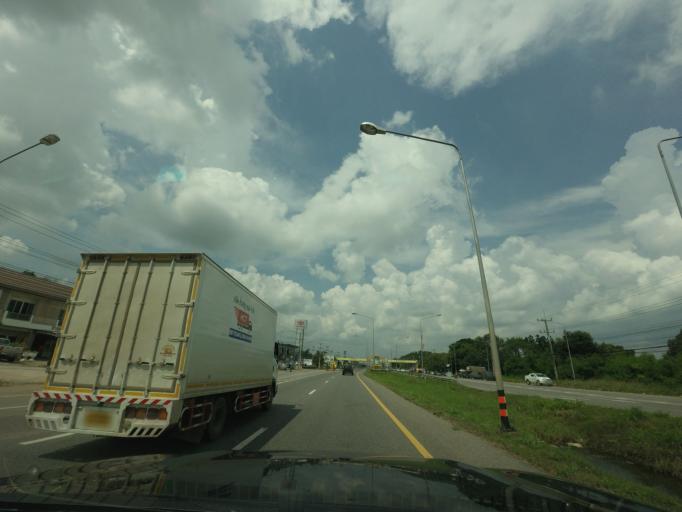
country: TH
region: Khon Kaen
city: Nong Ruea
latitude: 16.4902
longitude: 102.4452
